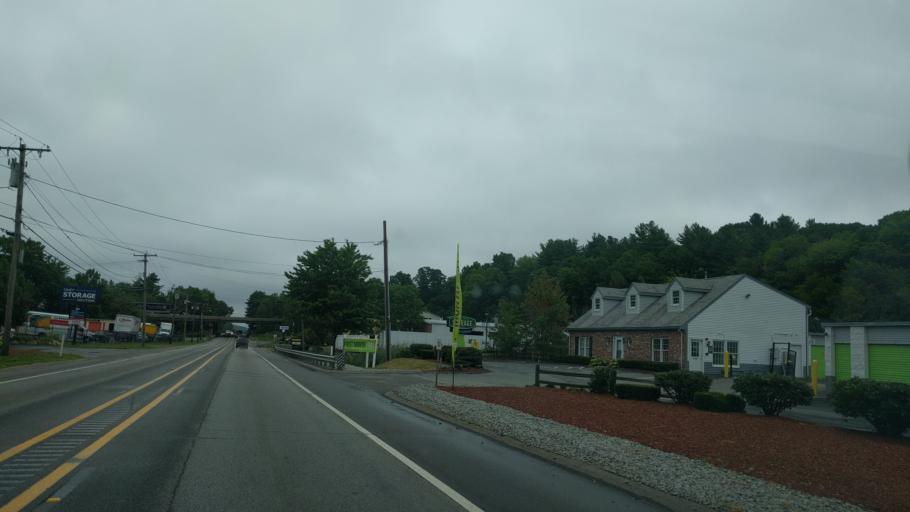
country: US
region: Massachusetts
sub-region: Worcester County
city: Auburn
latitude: 42.2019
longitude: -71.8157
